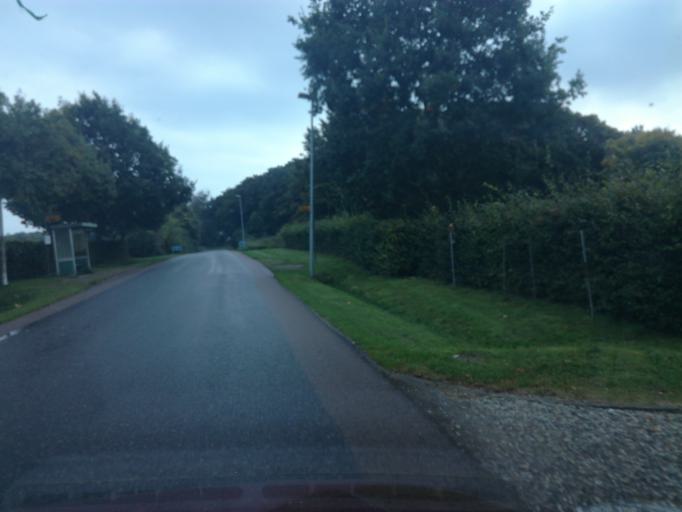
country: DK
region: South Denmark
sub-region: Fredericia Kommune
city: Fredericia
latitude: 55.6248
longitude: 9.8328
